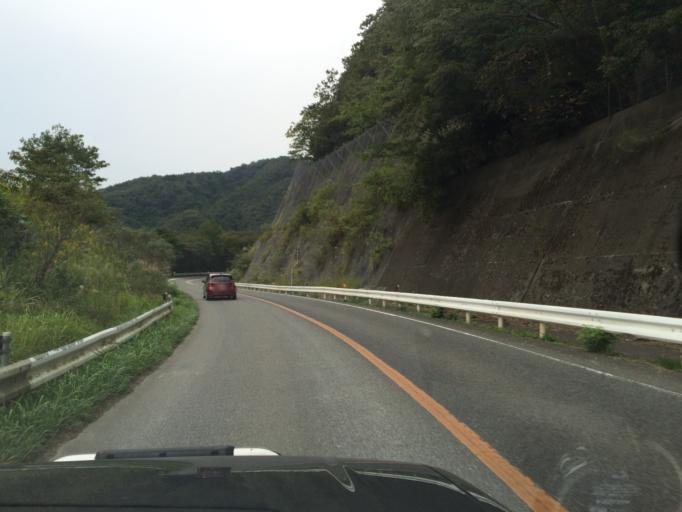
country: JP
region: Hyogo
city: Toyooka
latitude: 35.4061
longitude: 134.7823
